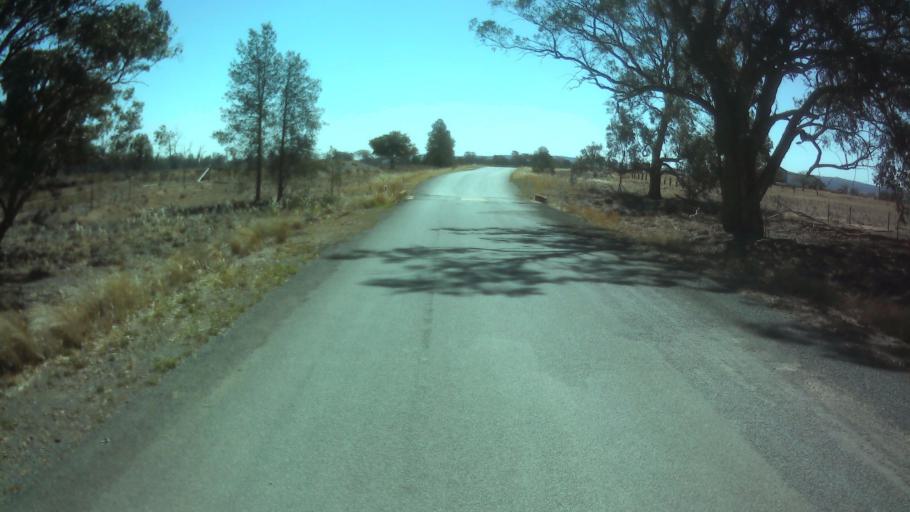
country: AU
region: New South Wales
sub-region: Weddin
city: Grenfell
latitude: -33.8163
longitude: 147.9417
